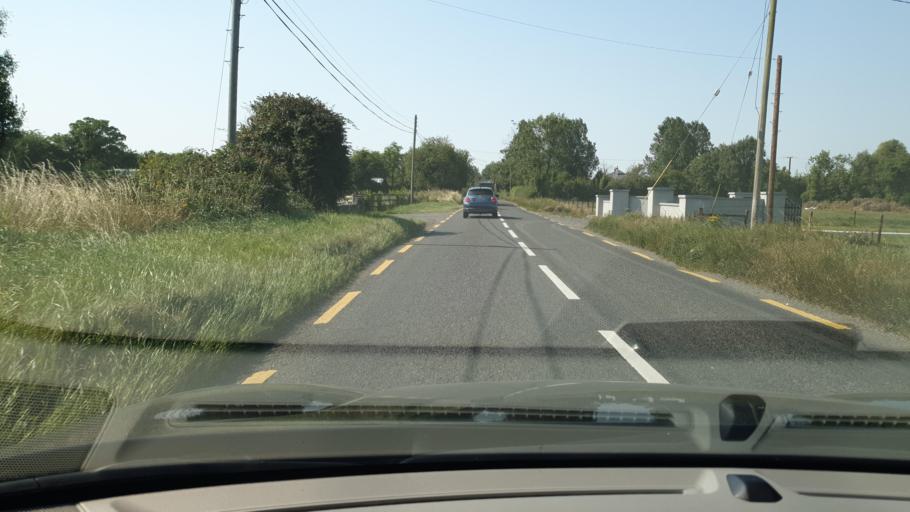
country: IE
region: Leinster
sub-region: An Mhi
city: Trim
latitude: 53.5765
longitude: -6.8338
